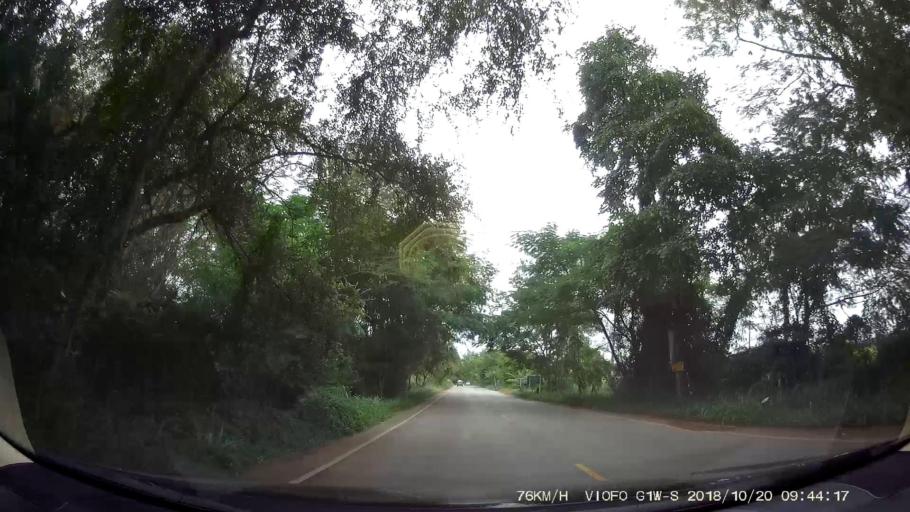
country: TH
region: Chaiyaphum
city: Khon San
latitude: 16.4816
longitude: 101.9445
